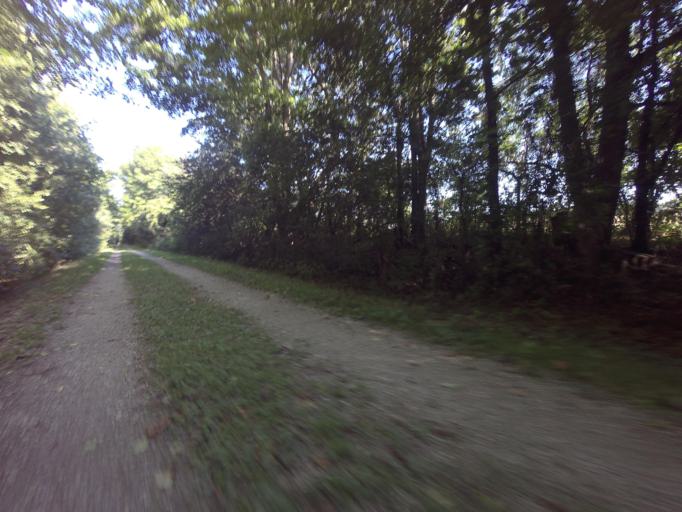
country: CA
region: Ontario
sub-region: Wellington County
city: Guelph
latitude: 43.6550
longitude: -80.4218
